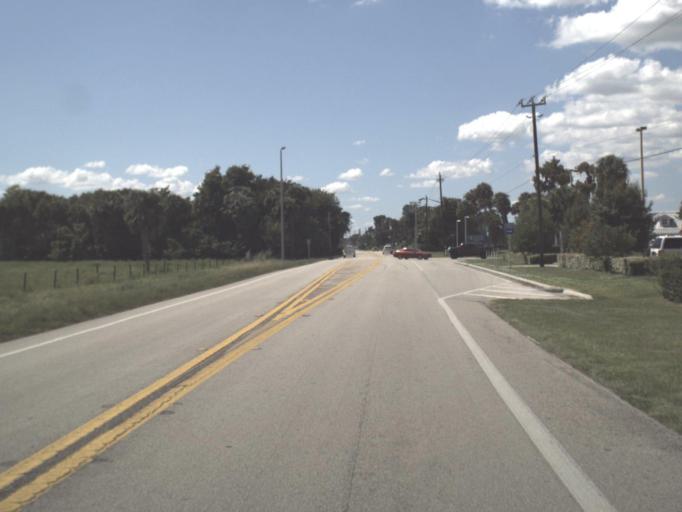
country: US
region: Florida
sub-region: Okeechobee County
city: Taylor Creek
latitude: 27.2075
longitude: -80.8080
